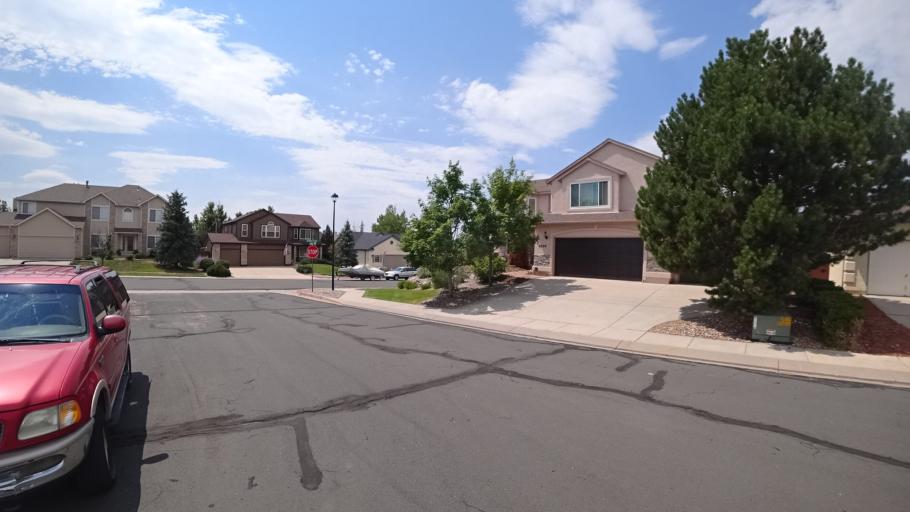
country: US
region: Colorado
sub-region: El Paso County
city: Air Force Academy
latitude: 38.9661
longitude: -104.7799
